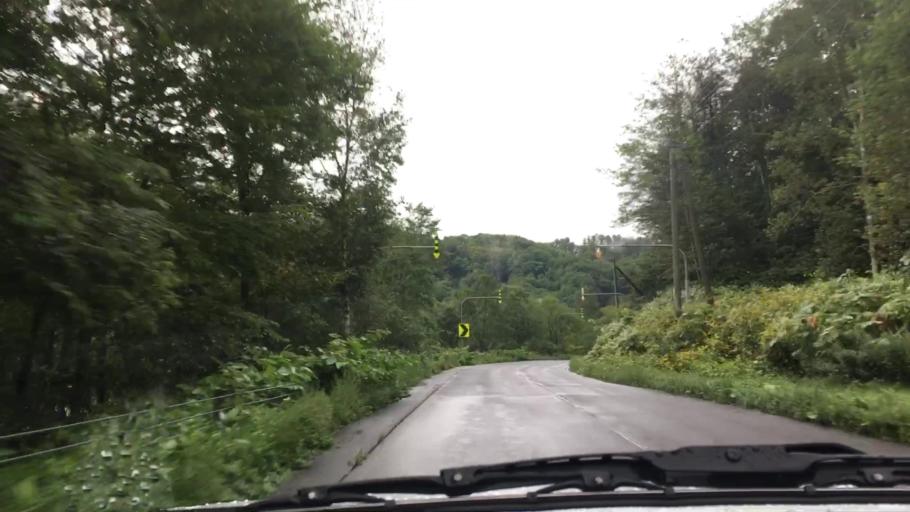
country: JP
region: Hokkaido
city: Niseko Town
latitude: 42.6672
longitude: 140.7776
